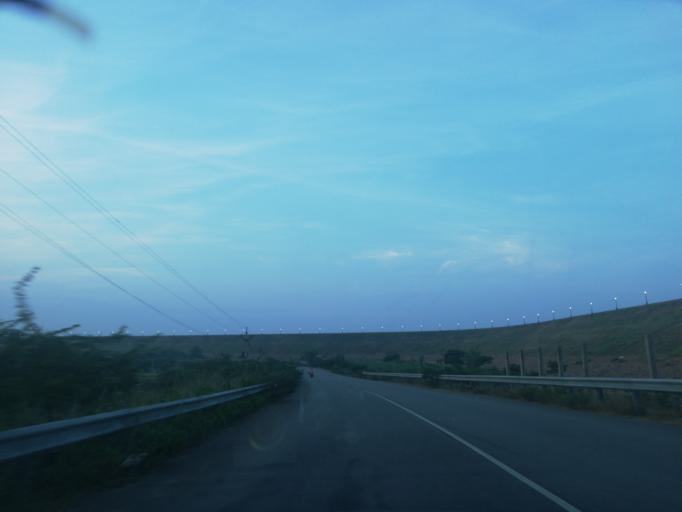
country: IN
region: Andhra Pradesh
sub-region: Guntur
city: Macherla
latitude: 16.5980
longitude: 79.3073
